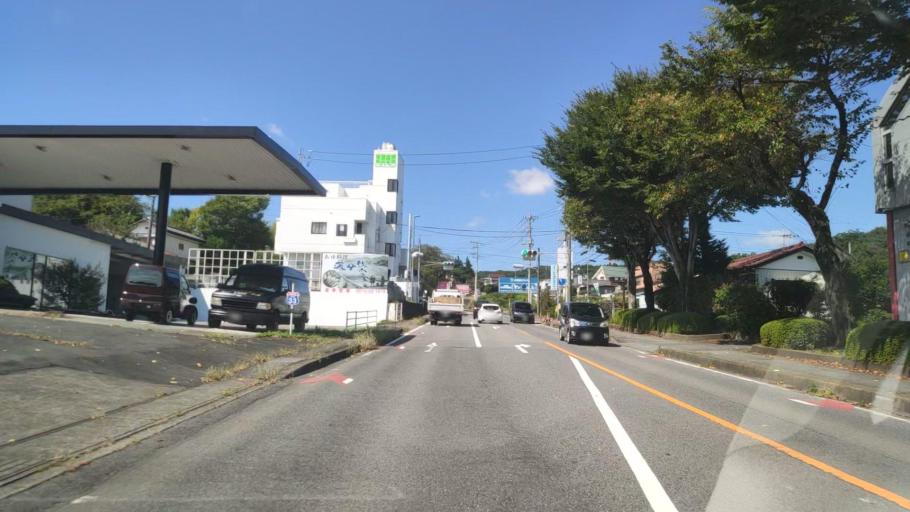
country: JP
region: Gunma
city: Shibukawa
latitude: 36.5031
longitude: 138.9802
